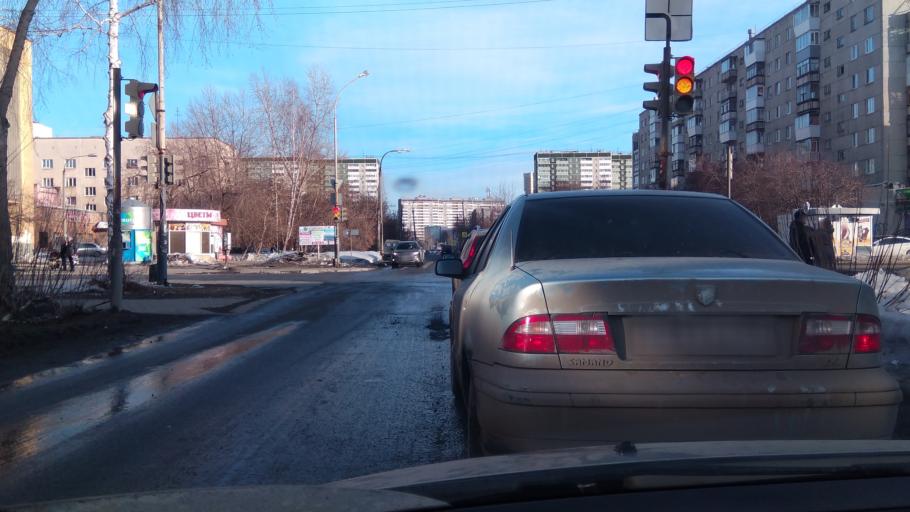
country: RU
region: Sverdlovsk
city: Shuvakish
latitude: 56.8679
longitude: 60.5359
